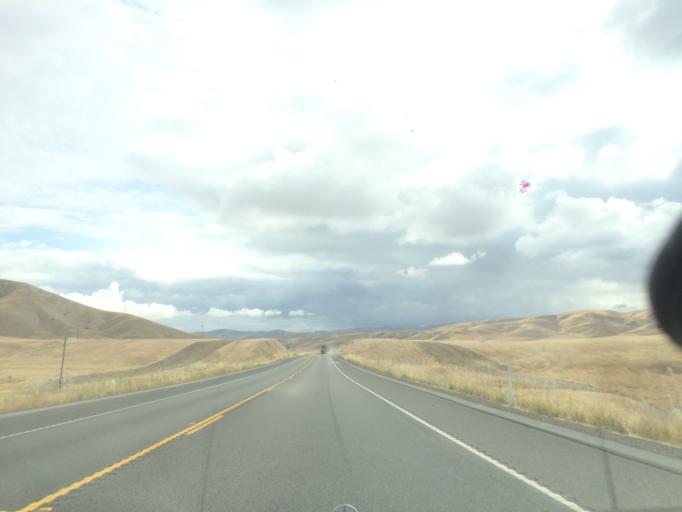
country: US
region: California
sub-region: San Luis Obispo County
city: Shandon
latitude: 35.7134
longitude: -120.3065
